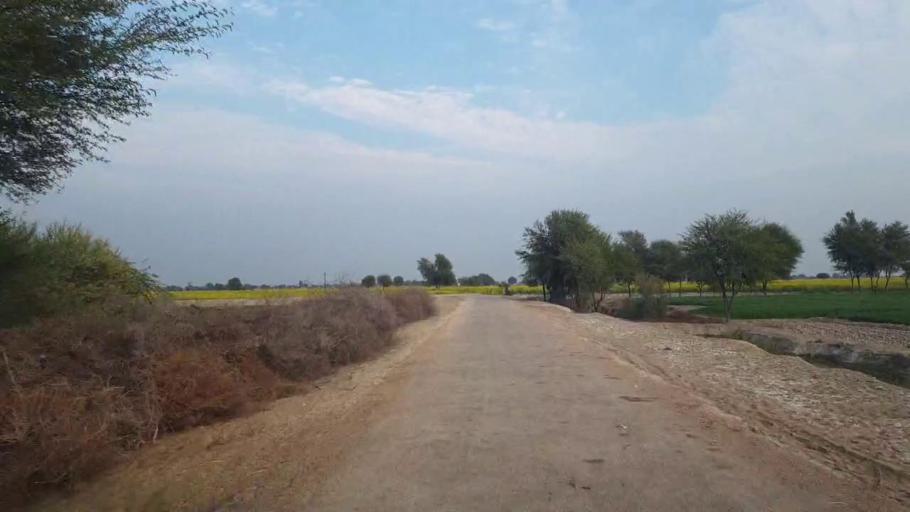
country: PK
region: Sindh
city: Shahpur Chakar
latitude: 26.0979
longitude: 68.5474
